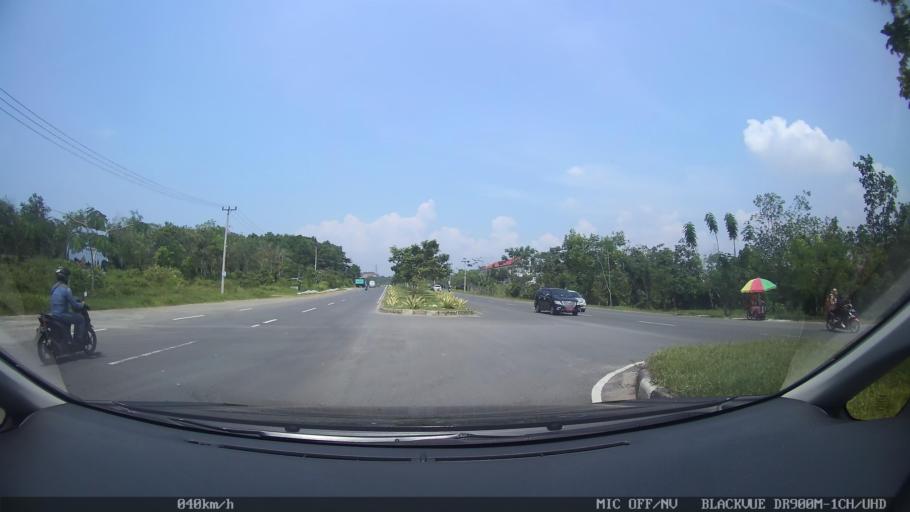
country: ID
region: Lampung
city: Kedaton
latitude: -5.3552
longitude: 105.3173
